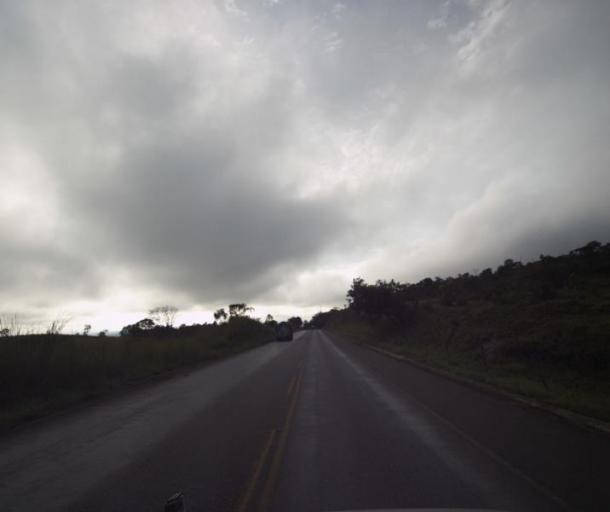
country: BR
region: Goias
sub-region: Pirenopolis
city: Pirenopolis
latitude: -15.7534
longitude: -48.7366
